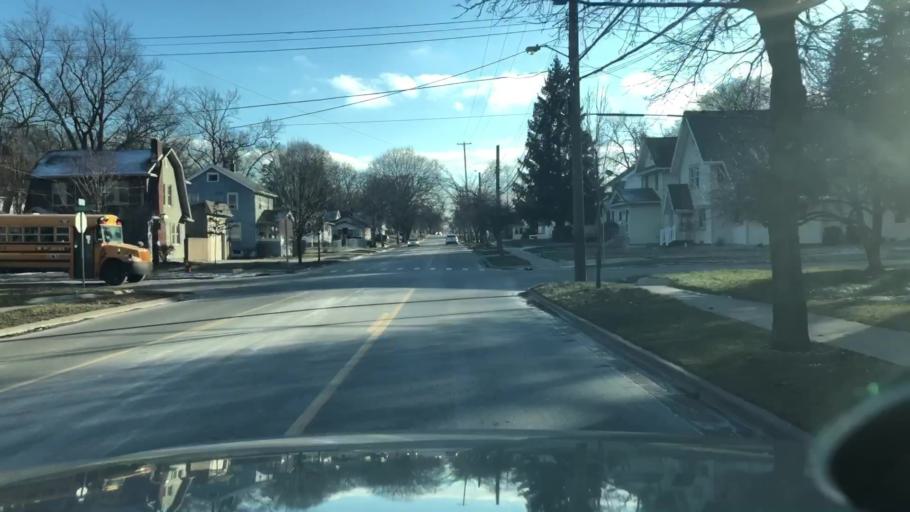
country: US
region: Michigan
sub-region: Jackson County
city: Jackson
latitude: 42.2368
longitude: -84.4233
